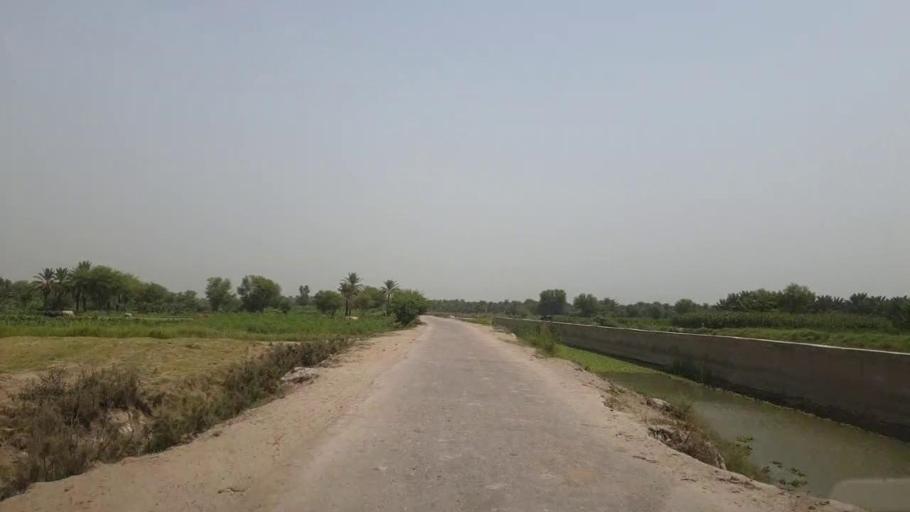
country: PK
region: Sindh
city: Gambat
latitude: 27.4297
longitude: 68.5606
